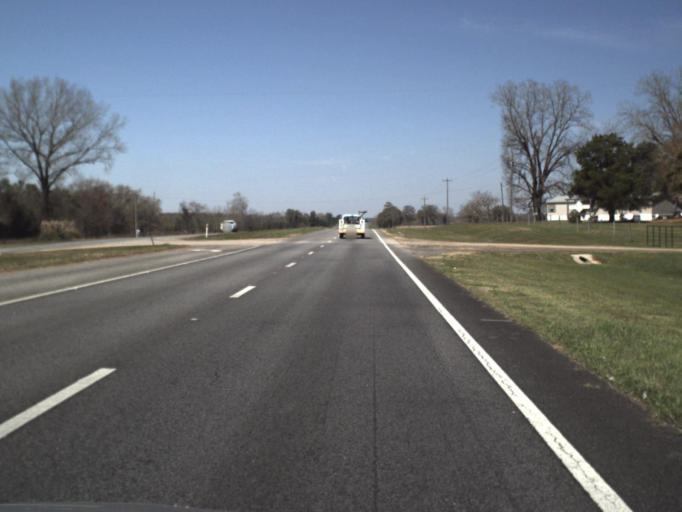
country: US
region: Florida
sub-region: Jackson County
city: Graceville
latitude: 30.8940
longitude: -85.3705
